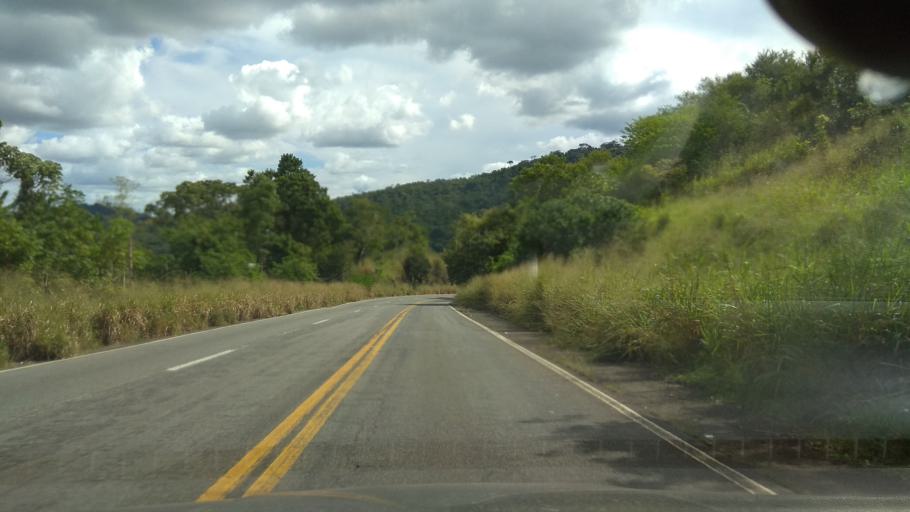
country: BR
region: Bahia
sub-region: Ubaitaba
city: Ubaitaba
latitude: -14.2528
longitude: -39.3724
